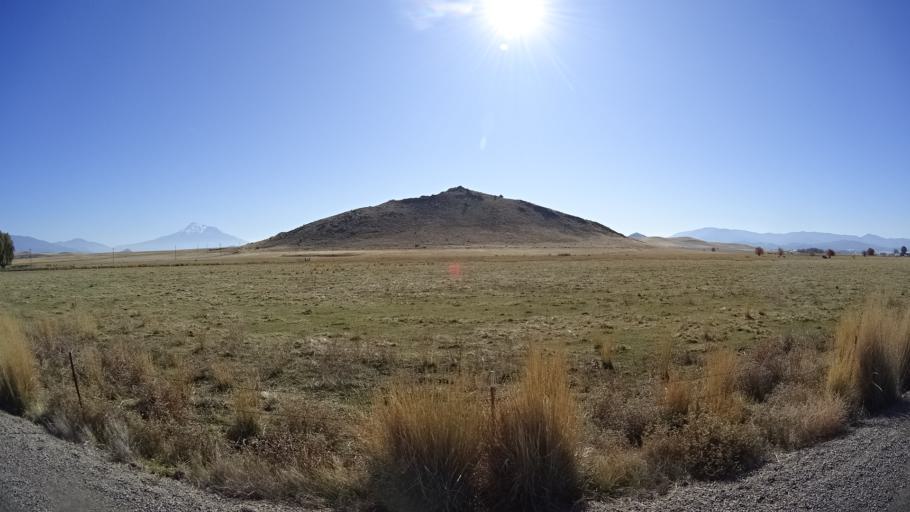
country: US
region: California
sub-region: Siskiyou County
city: Montague
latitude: 41.7563
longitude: -122.4884
